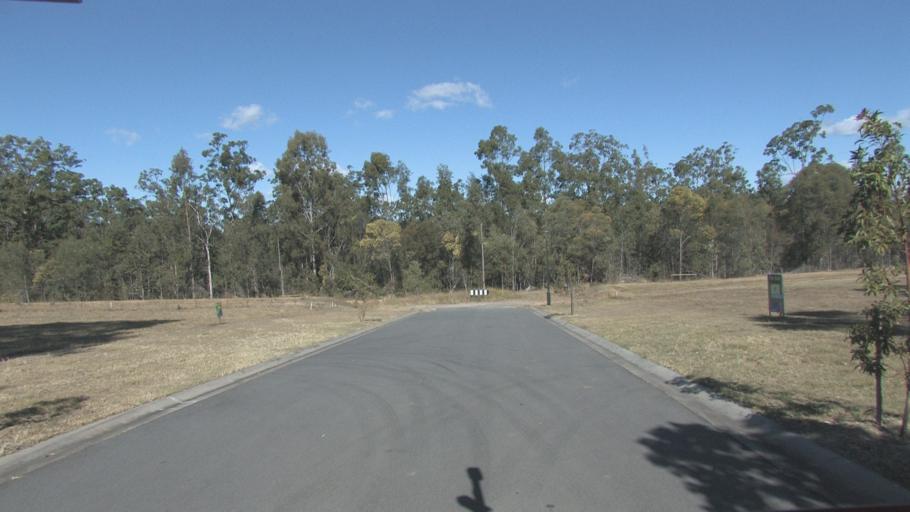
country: AU
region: Queensland
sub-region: Logan
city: North Maclean
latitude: -27.7607
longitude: 152.9499
